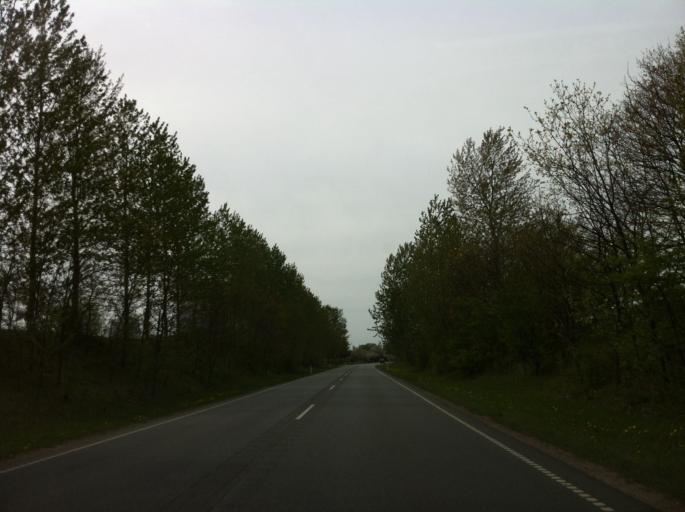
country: DK
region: Capital Region
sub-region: Hillerod Kommune
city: Hillerod
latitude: 55.9113
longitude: 12.3135
